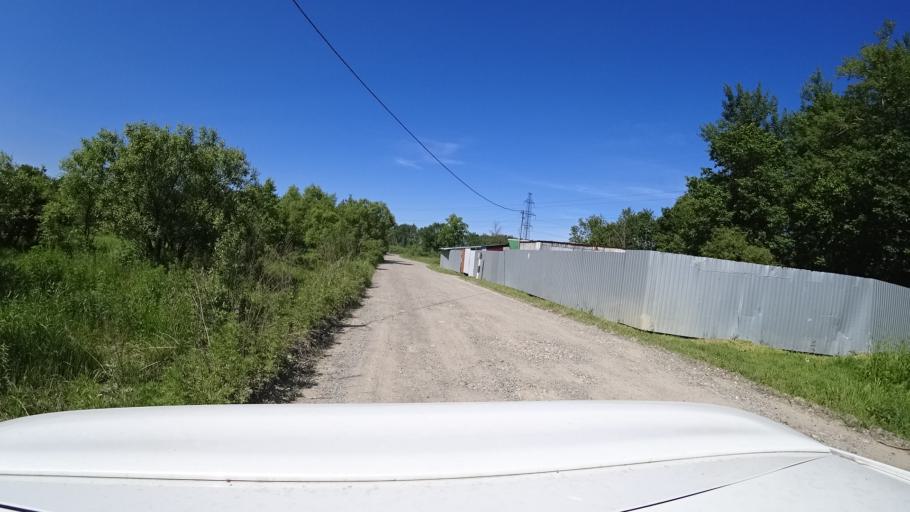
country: RU
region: Khabarovsk Krai
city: Topolevo
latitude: 48.5647
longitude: 135.1972
